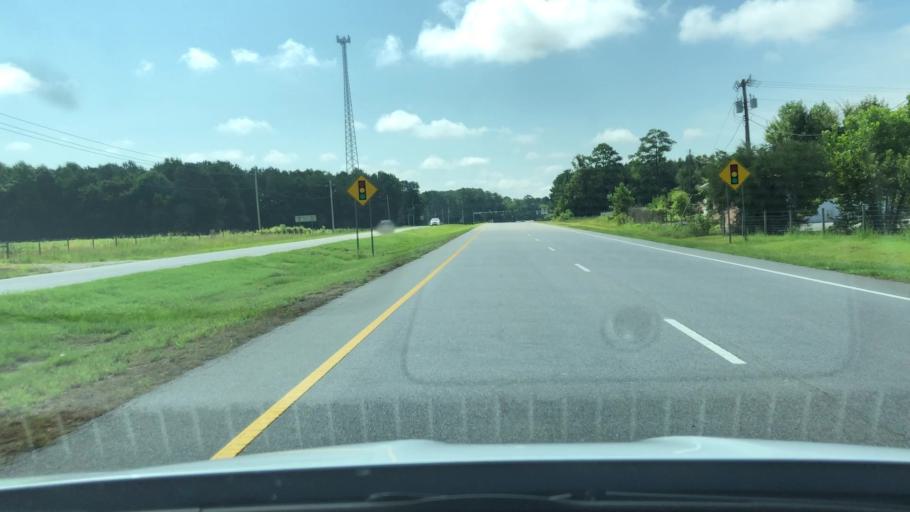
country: US
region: North Carolina
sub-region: Bertie County
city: Windsor
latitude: 35.9885
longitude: -76.9607
